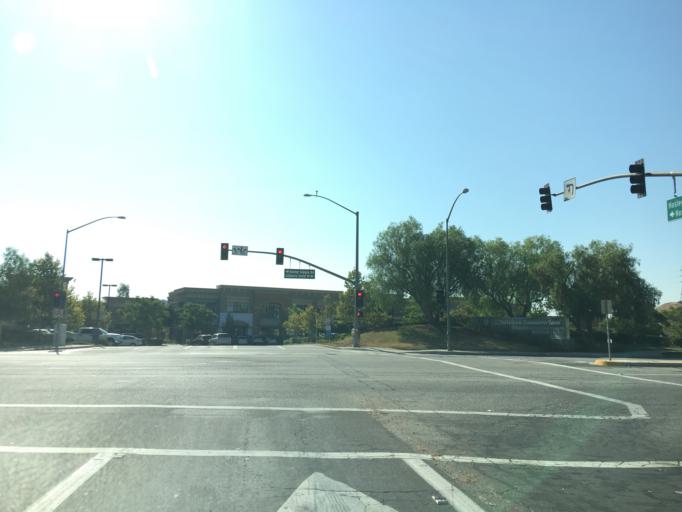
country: US
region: California
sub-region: Los Angeles County
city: Valencia
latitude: 34.4511
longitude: -118.6259
